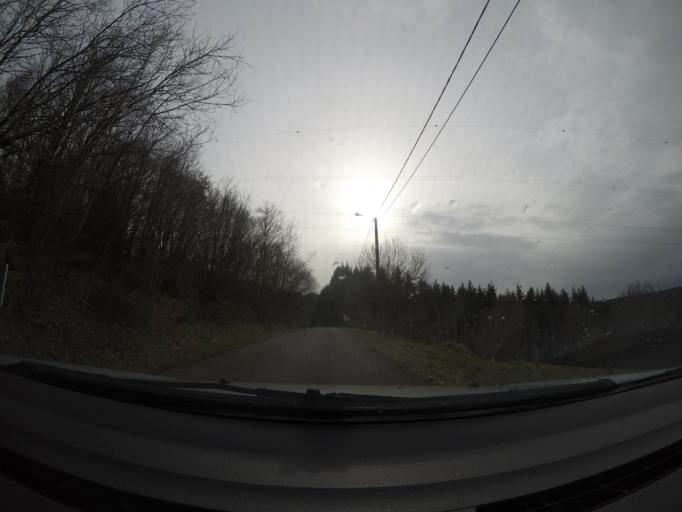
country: BE
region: Wallonia
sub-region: Province du Luxembourg
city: Martelange
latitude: 49.8244
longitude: 5.7227
